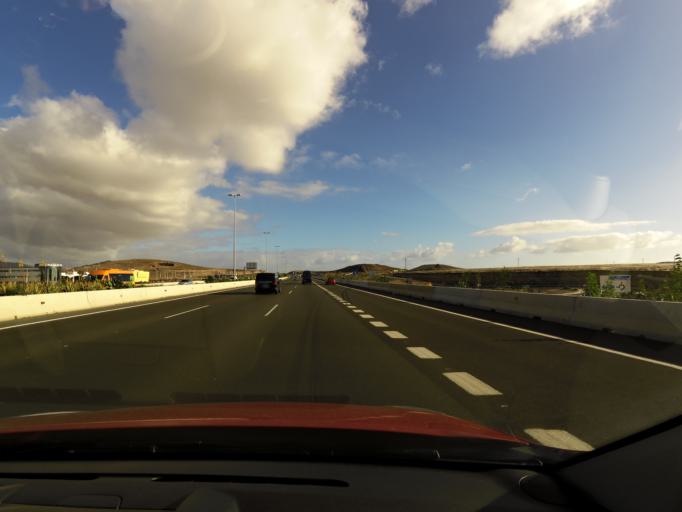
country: ES
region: Canary Islands
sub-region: Provincia de Las Palmas
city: Cruce de Arinaga
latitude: 27.8736
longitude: -15.4164
